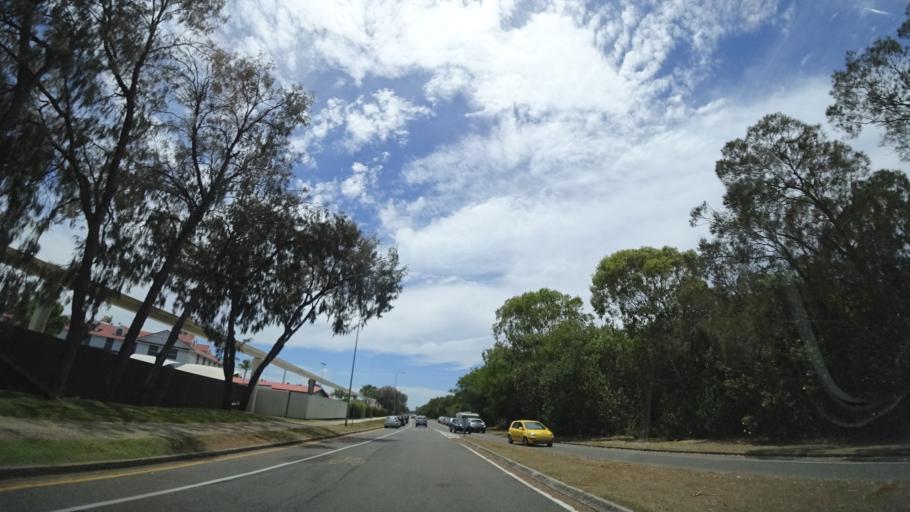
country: AU
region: Queensland
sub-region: Gold Coast
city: Main Beach
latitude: -27.9610
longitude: 153.4267
